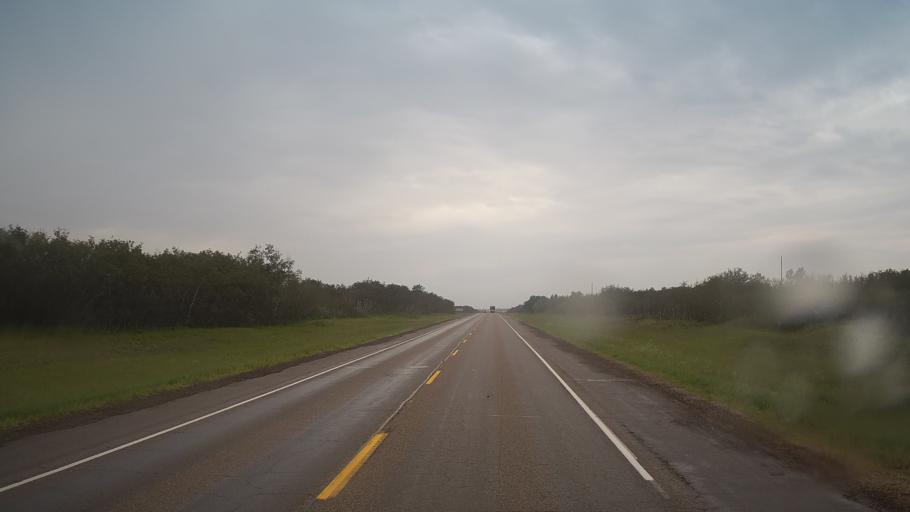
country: CA
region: Saskatchewan
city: Langham
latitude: 52.1294
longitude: -107.0394
